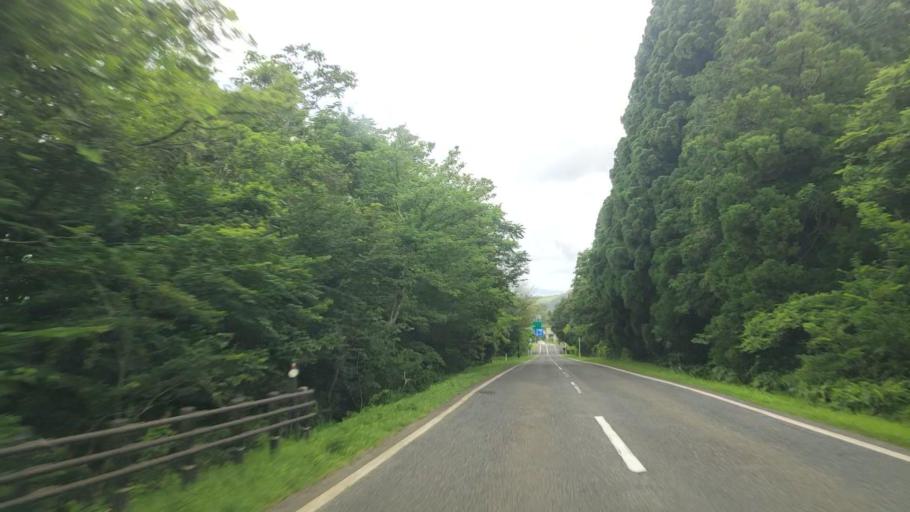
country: JP
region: Tottori
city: Yonago
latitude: 35.4062
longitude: 133.4821
